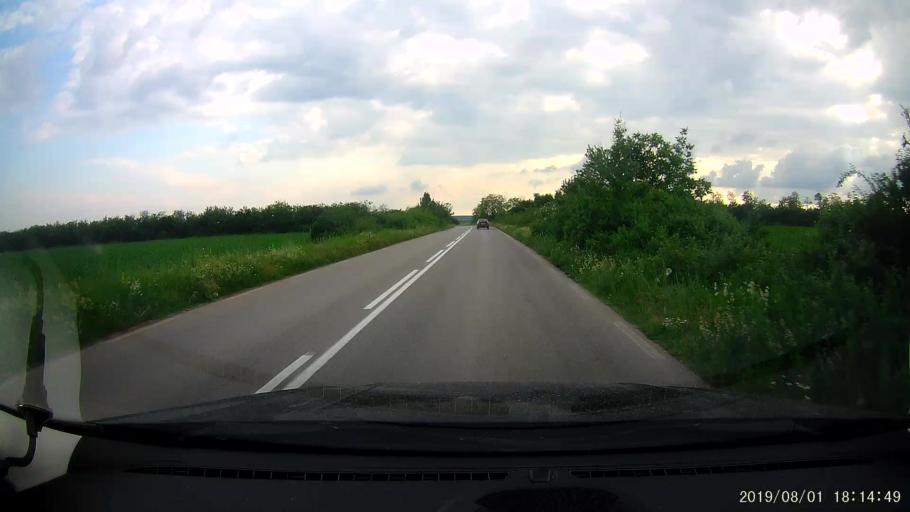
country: BG
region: Silistra
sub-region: Obshtina Dulovo
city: Dulovo
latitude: 43.7629
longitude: 27.1180
